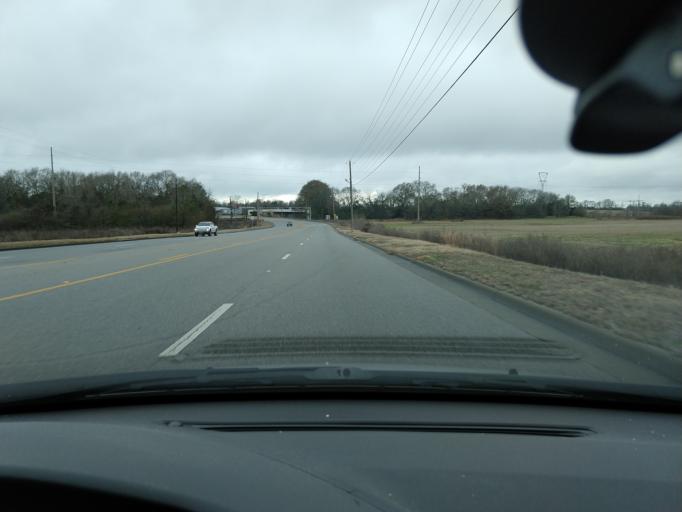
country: US
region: Alabama
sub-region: Houston County
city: Dothan
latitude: 31.2718
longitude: -85.4079
